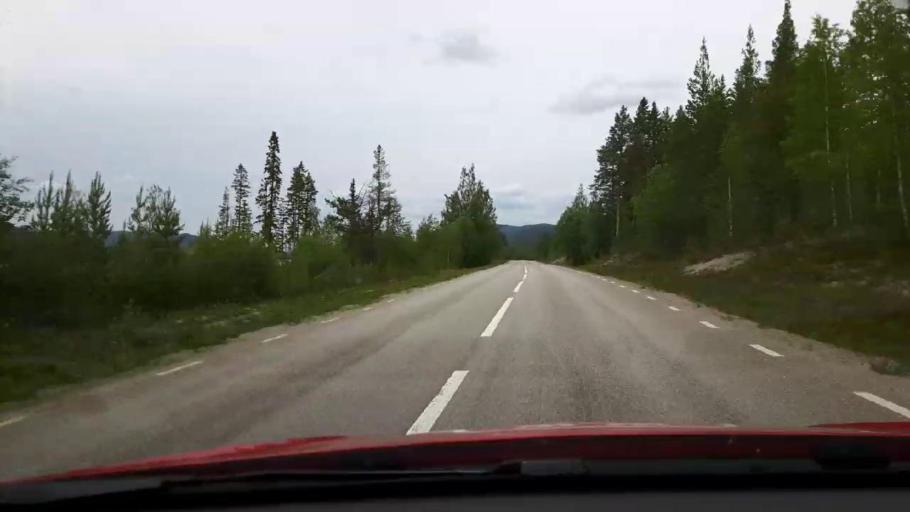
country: SE
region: Jaemtland
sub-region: Harjedalens Kommun
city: Sveg
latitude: 62.2631
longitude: 13.8385
